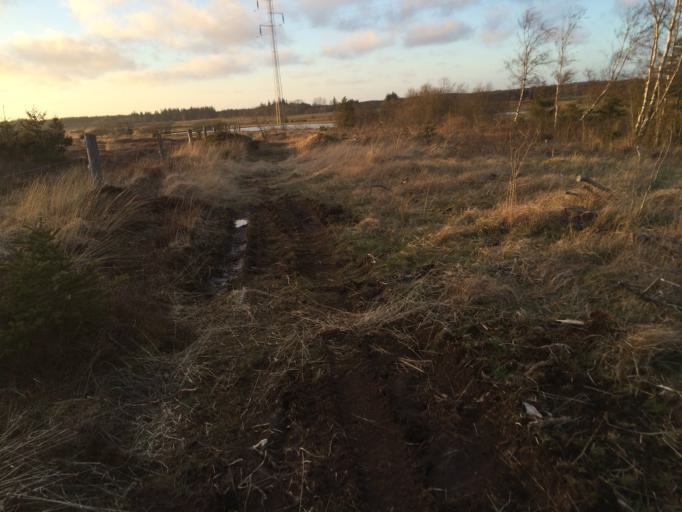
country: DK
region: Central Jutland
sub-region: Holstebro Kommune
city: Ulfborg
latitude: 56.2452
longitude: 8.4082
